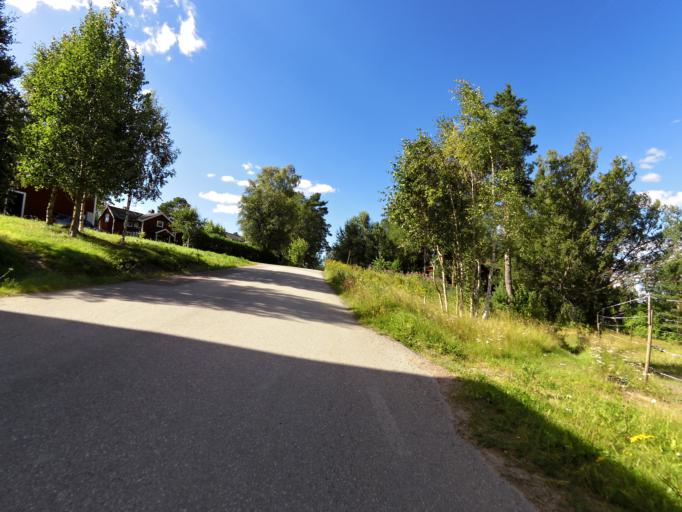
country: SE
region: Dalarna
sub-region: Faluns Kommun
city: Svardsjo
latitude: 60.6415
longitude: 15.8473
